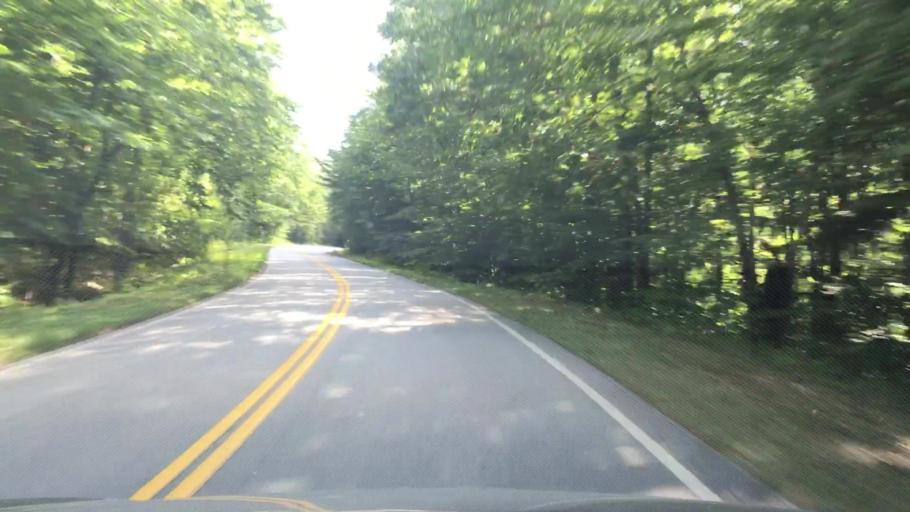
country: US
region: New Hampshire
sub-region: Carroll County
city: North Conway
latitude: 44.0491
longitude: -71.2765
